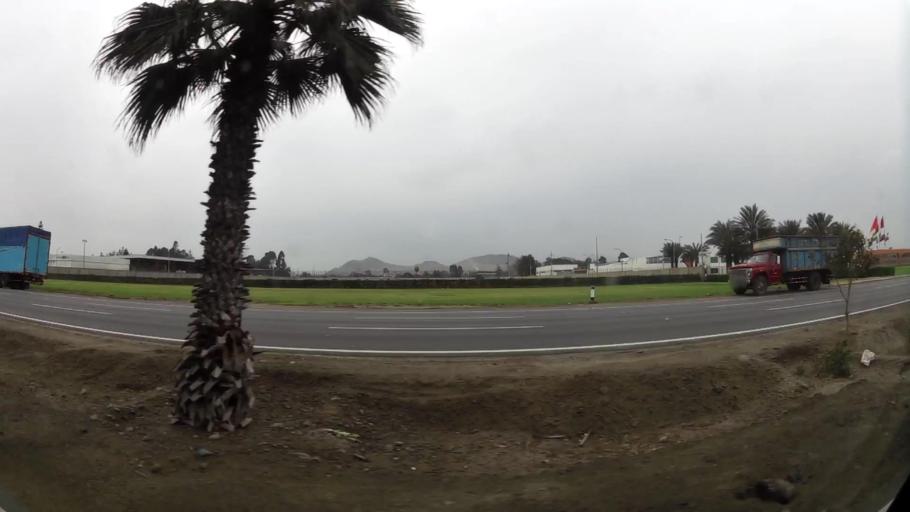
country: PE
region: Lima
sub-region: Lima
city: Punta Hermosa
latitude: -12.2812
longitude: -76.8815
